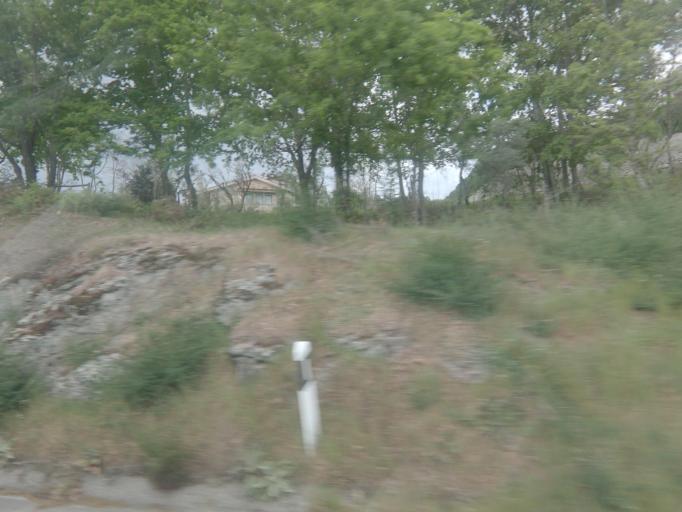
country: PT
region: Porto
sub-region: Amarante
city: Amarante
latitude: 41.2748
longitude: -8.0043
